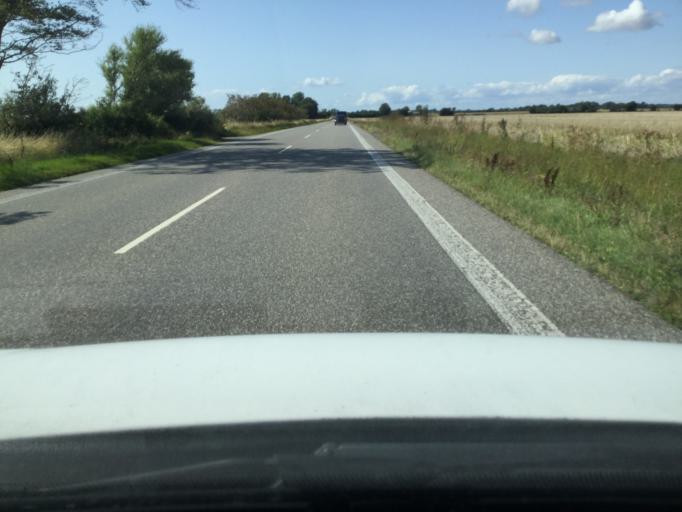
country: DK
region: Zealand
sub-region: Lolland Kommune
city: Nakskov
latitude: 54.8056
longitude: 11.2307
